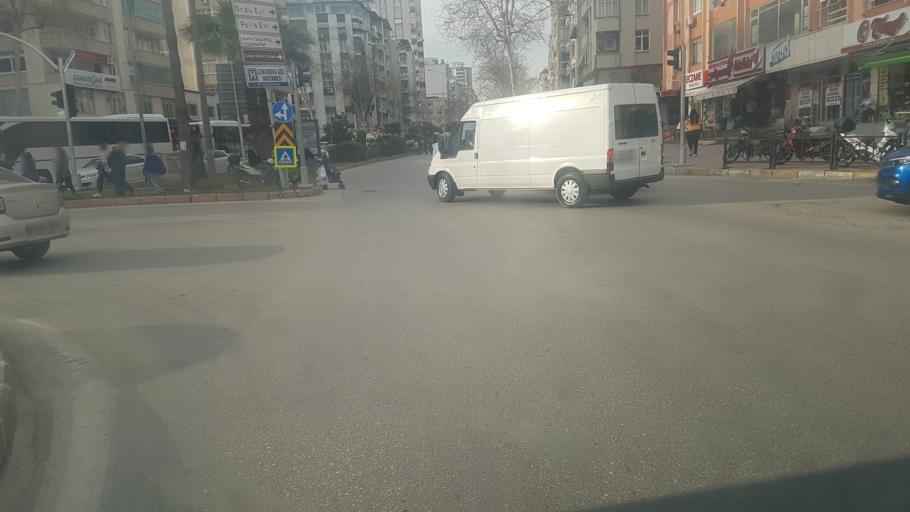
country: TR
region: Adana
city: Adana
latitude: 37.0225
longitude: 35.3155
